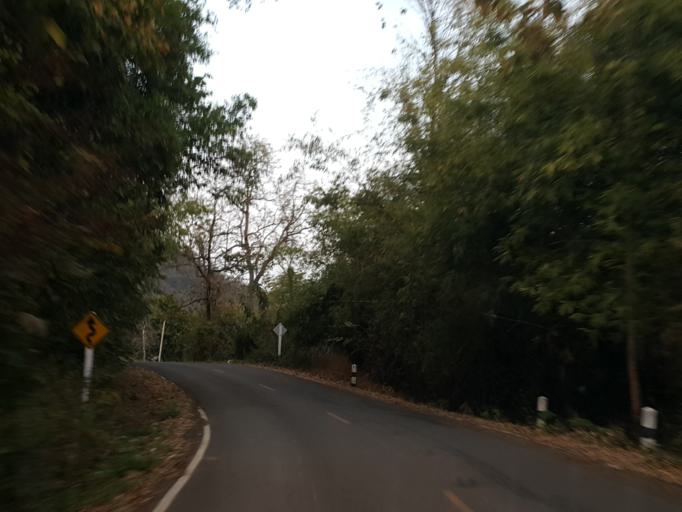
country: TH
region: Lampang
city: Mueang Pan
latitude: 18.8236
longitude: 99.4548
